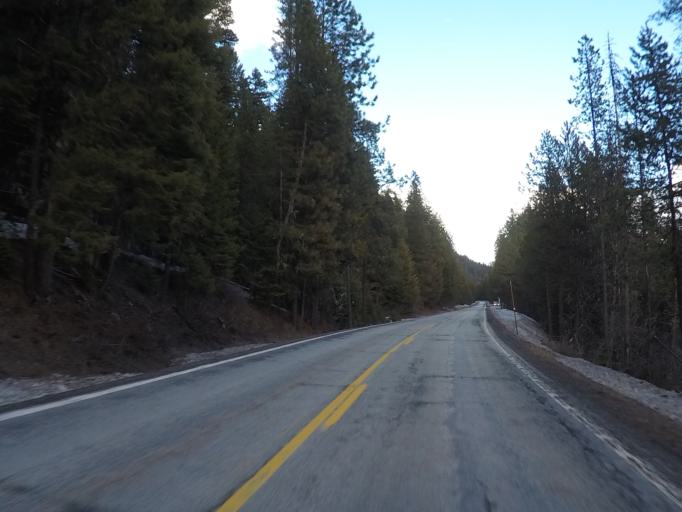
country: US
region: Montana
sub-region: Ravalli County
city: Hamilton
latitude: 46.5168
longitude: -114.7549
